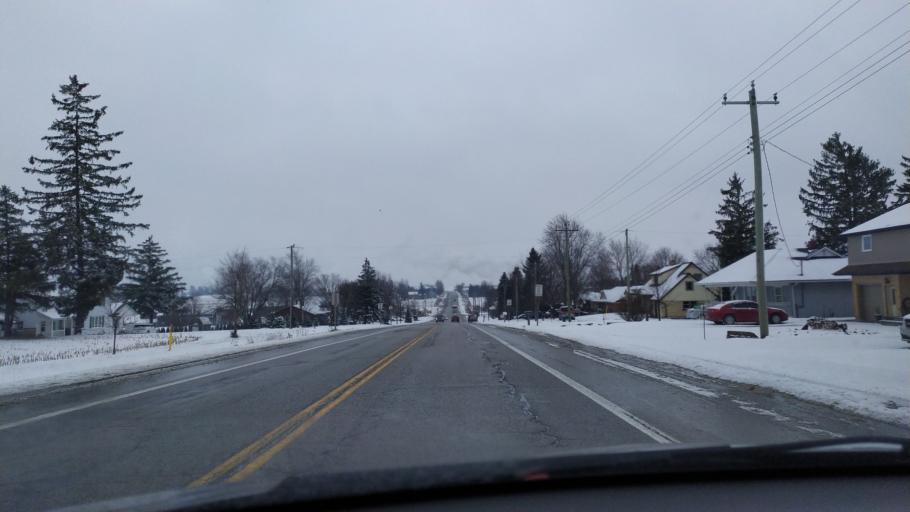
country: CA
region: Ontario
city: Waterloo
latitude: 43.5969
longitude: -80.6273
